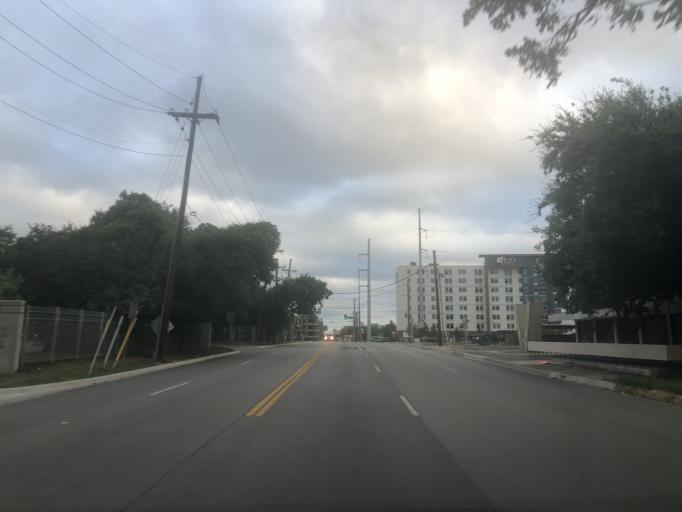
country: US
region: Texas
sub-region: Dallas County
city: University Park
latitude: 32.8247
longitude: -96.8465
